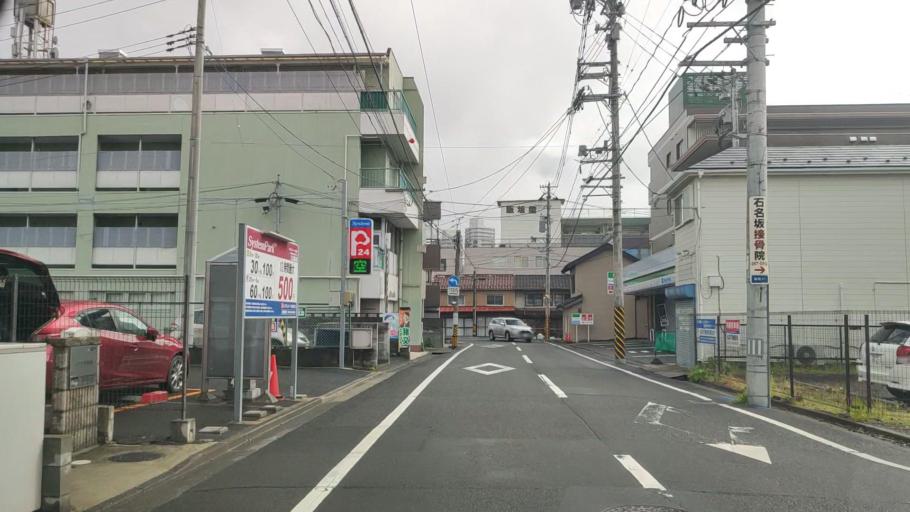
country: JP
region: Miyagi
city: Sendai
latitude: 38.2450
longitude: 140.8891
